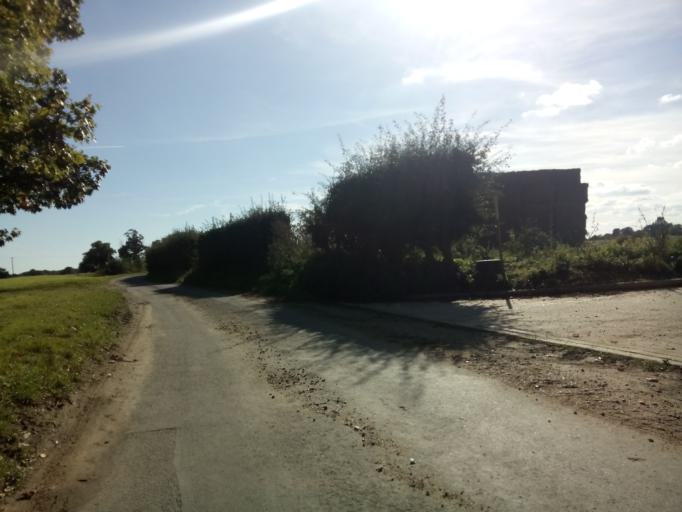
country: GB
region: England
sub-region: Suffolk
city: Ipswich
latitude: 52.0202
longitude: 1.1406
